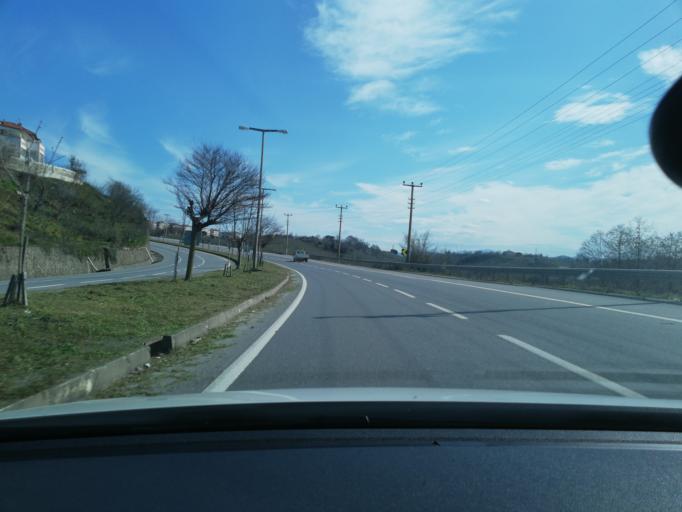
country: TR
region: Duzce
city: Akcakoca
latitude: 41.0828
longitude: 31.1591
